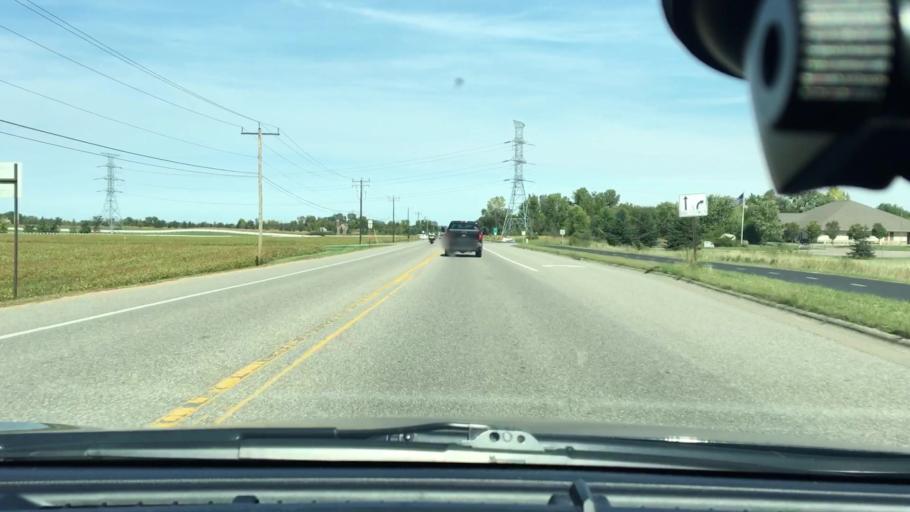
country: US
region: Minnesota
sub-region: Wright County
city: Hanover
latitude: 45.1259
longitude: -93.6357
